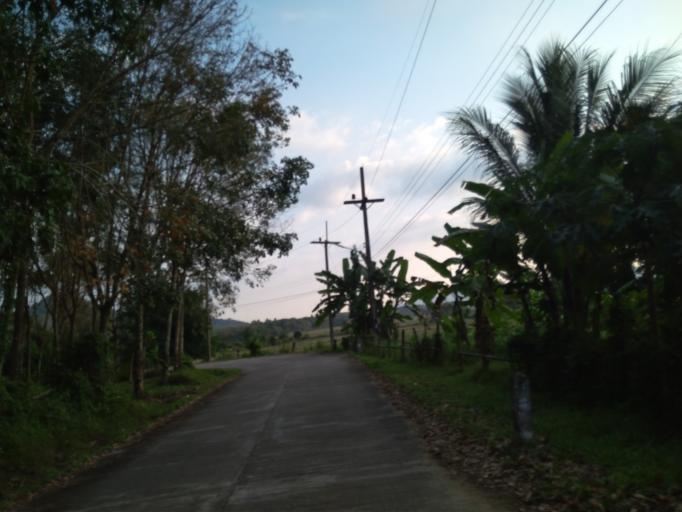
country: TH
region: Phangnga
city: Ko Yao
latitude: 8.1367
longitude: 98.5986
